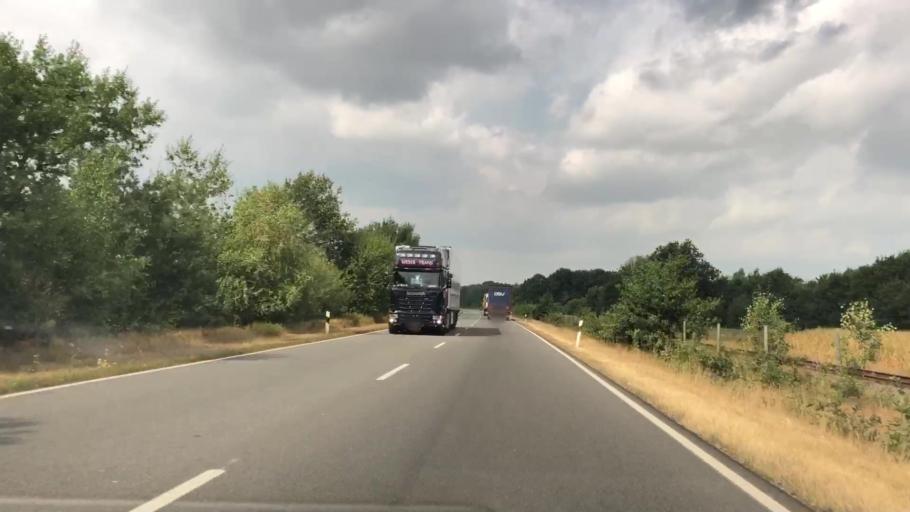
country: DE
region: Lower Saxony
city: Herzlake
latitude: 52.6950
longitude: 7.5917
